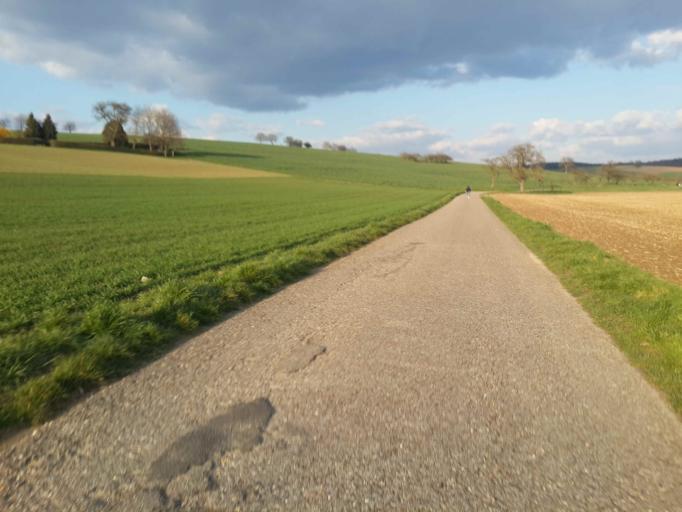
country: DE
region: Baden-Wuerttemberg
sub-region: Karlsruhe Region
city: Sinsheim
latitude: 49.2333
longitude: 8.9164
